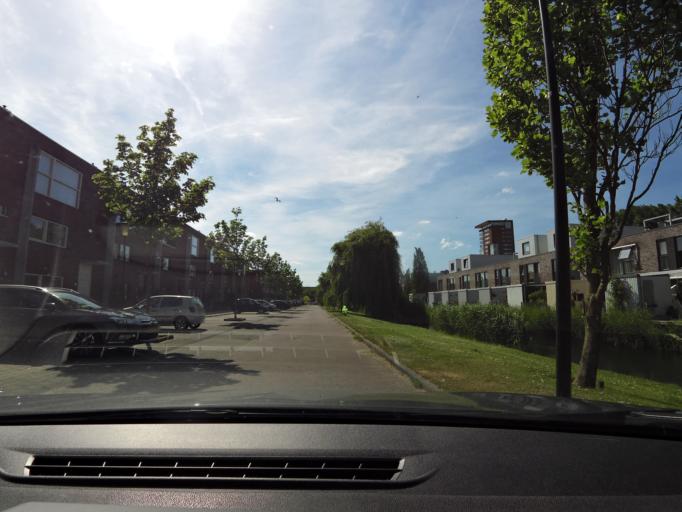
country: NL
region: South Holland
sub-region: Gemeente Barendrecht
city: Barendrecht
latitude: 51.8470
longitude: 4.5054
